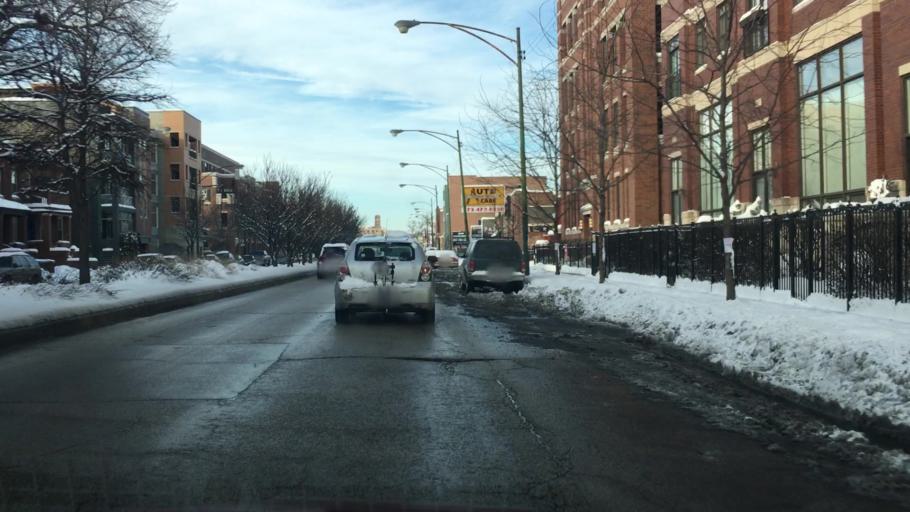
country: US
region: Illinois
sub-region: Cook County
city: Chicago
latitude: 41.9302
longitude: -87.6682
